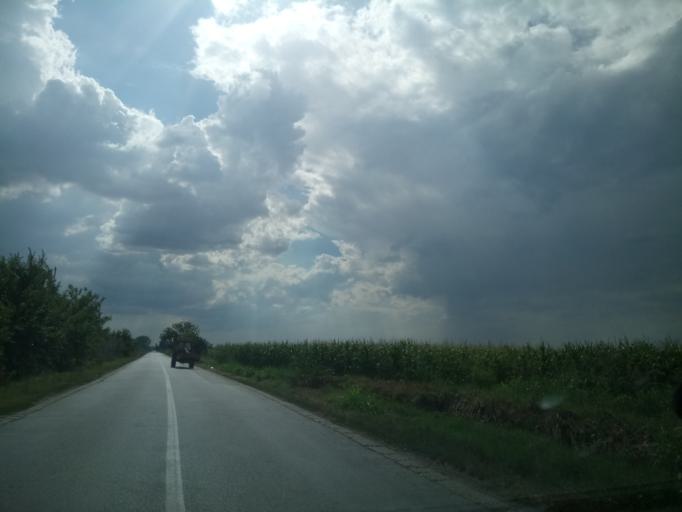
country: RS
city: Krcedin
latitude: 45.1380
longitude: 20.1087
